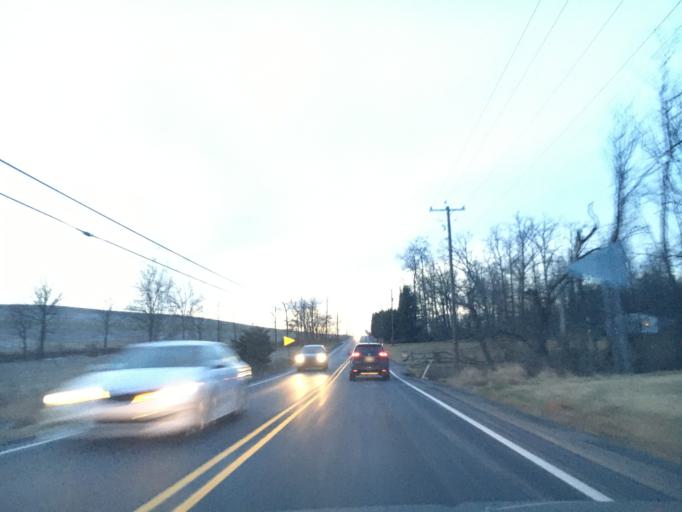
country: US
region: Pennsylvania
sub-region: Northampton County
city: Youngsville
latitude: 40.7525
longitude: -75.4870
